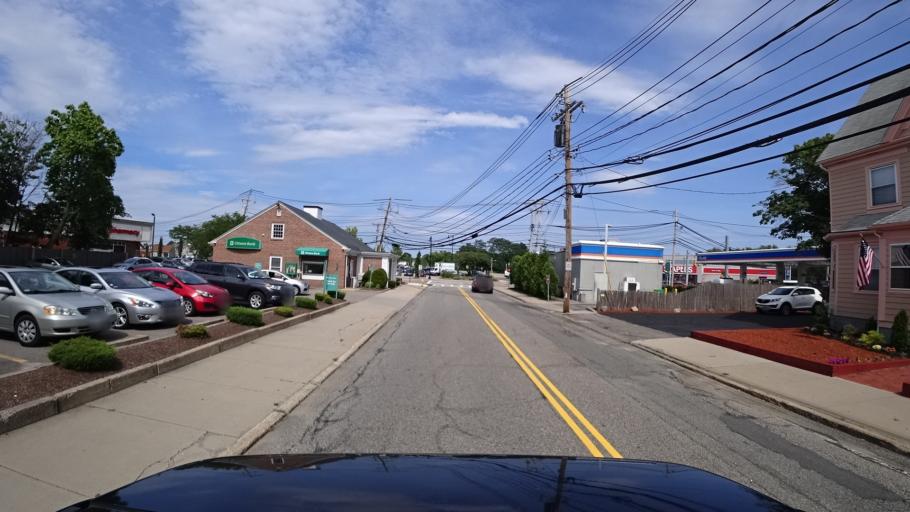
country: US
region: Massachusetts
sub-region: Norfolk County
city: Dedham
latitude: 42.2468
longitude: -71.1730
